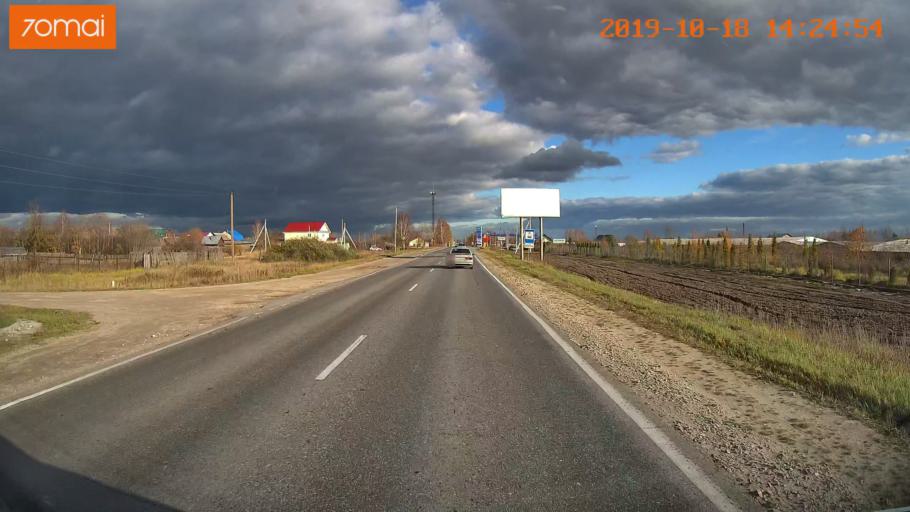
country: RU
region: Rjazan
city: Tuma
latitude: 55.1470
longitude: 40.5091
